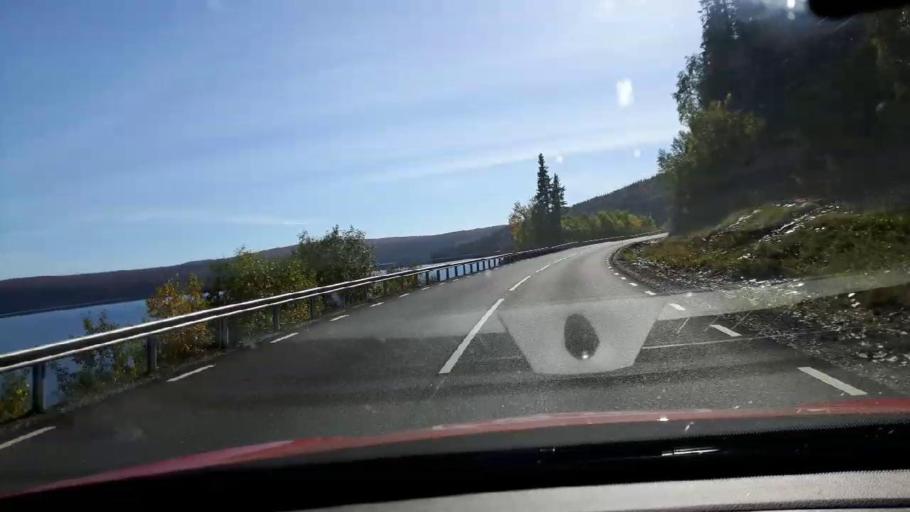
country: NO
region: Nord-Trondelag
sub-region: Royrvik
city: Royrvik
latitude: 64.8264
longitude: 14.0789
